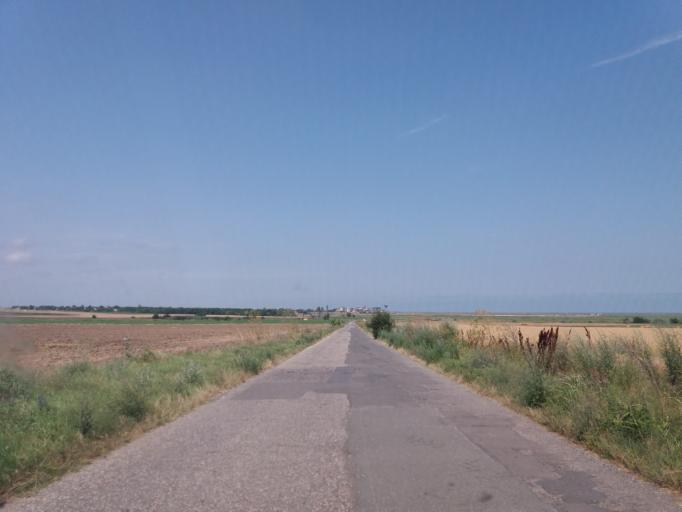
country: RO
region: Constanta
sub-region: Comuna Sacele
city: Sacele
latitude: 44.4344
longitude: 28.7207
